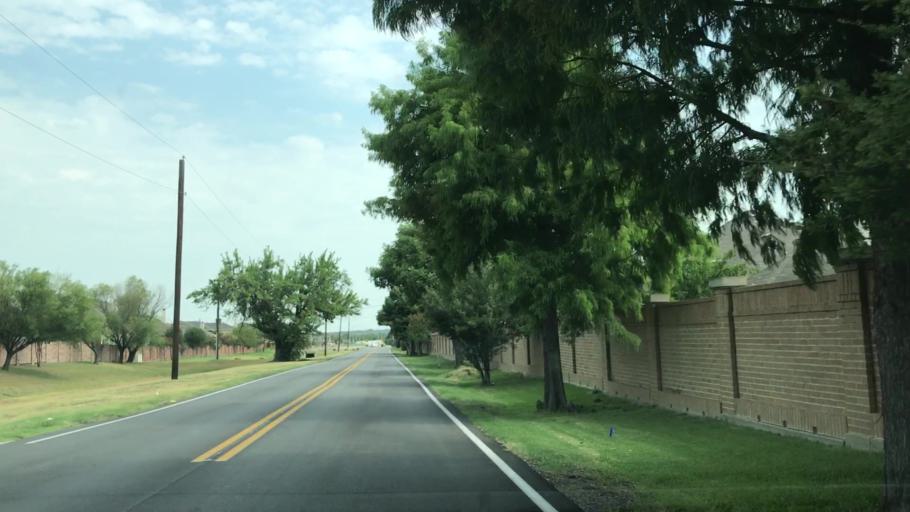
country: US
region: Texas
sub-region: Tarrant County
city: Keller
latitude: 32.9208
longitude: -97.2725
